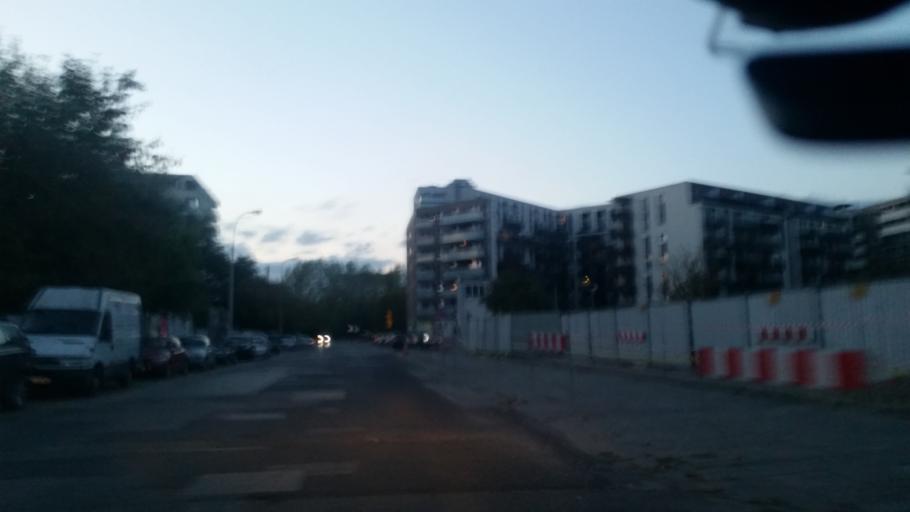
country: PL
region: Masovian Voivodeship
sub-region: Warszawa
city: Zoliborz
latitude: 52.2555
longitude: 20.9786
